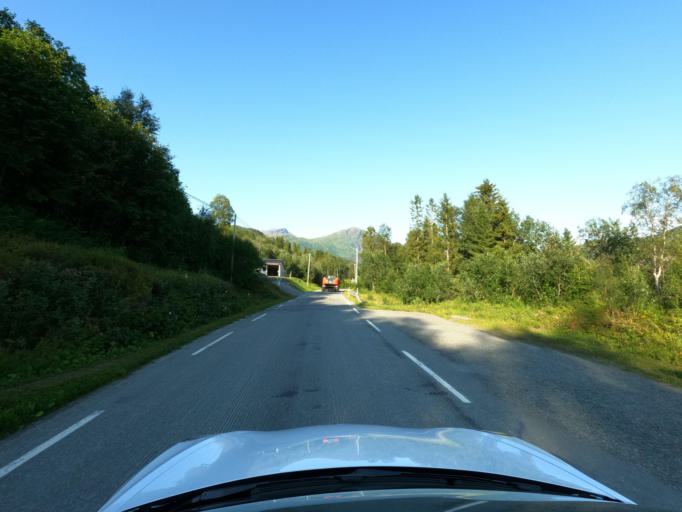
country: NO
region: Nordland
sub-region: Narvik
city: Bjerkvik
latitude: 68.5538
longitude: 17.5948
